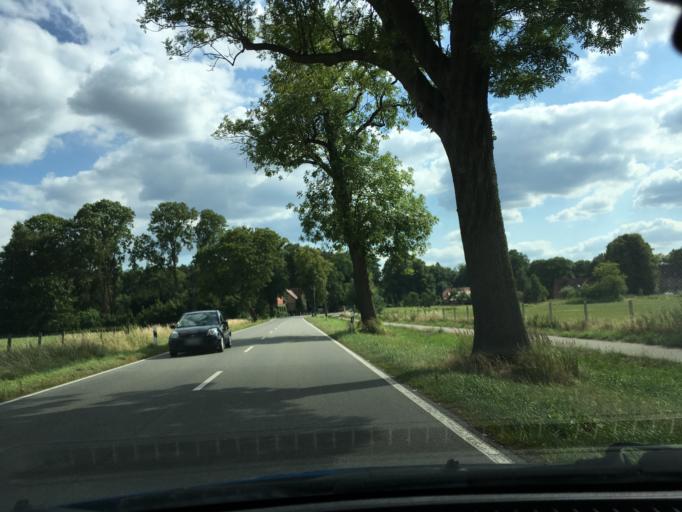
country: DE
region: Mecklenburg-Vorpommern
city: Lubtheen
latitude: 53.3357
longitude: 11.0778
